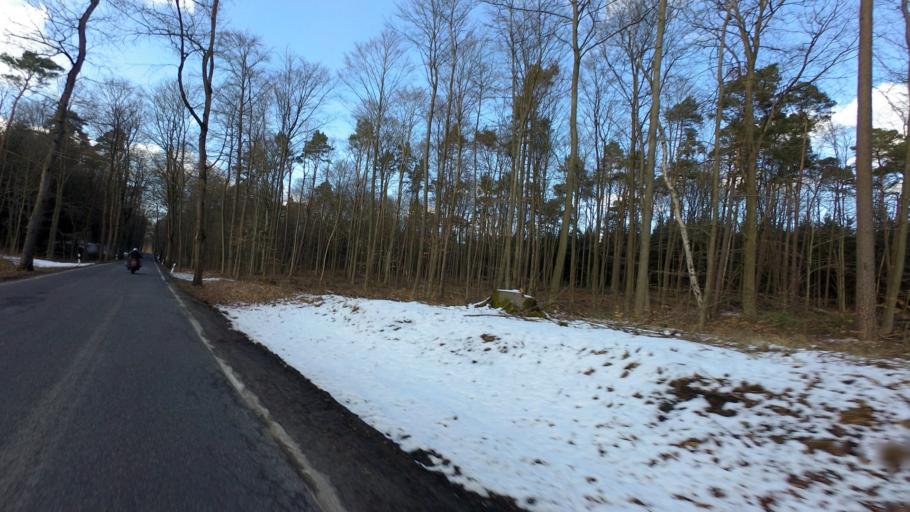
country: DE
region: Brandenburg
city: Wandlitz
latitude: 52.7635
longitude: 13.5196
